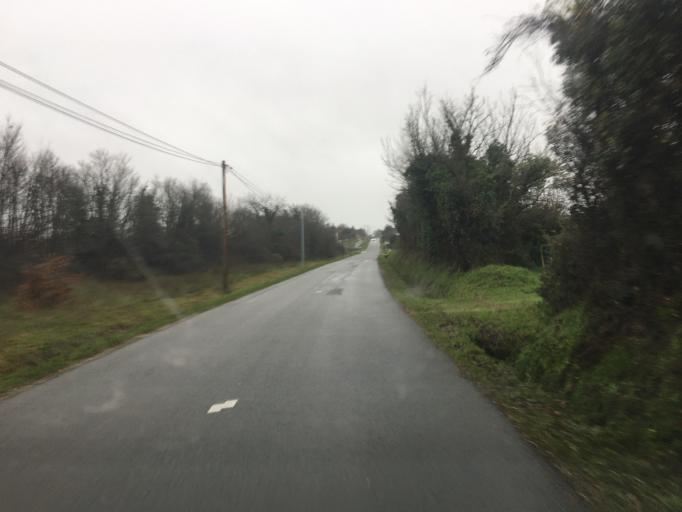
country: FR
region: Brittany
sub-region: Departement du Morbihan
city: Sarzeau
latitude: 47.5128
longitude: -2.6865
